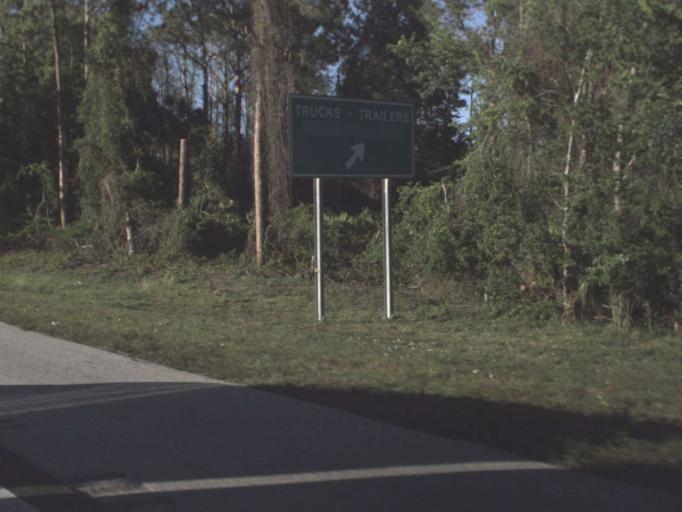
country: US
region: Florida
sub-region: Flagler County
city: Flagler Beach
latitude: 29.5007
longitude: -81.1930
